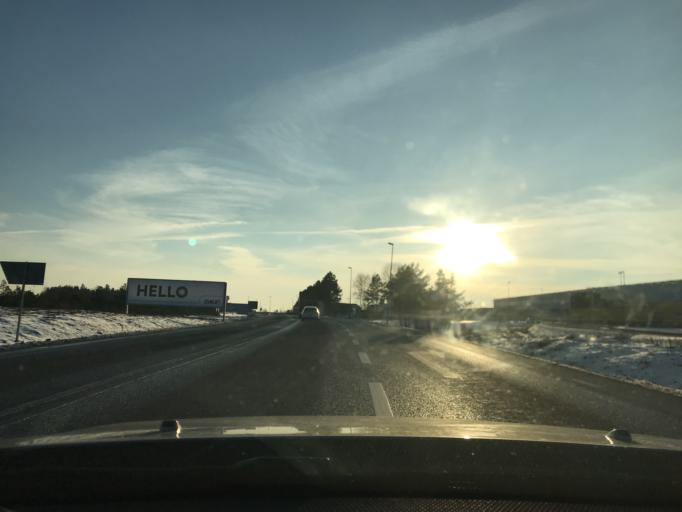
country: SE
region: Vaestra Goetaland
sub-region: Harryda Kommun
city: Landvetter
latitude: 57.6750
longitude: 12.3042
